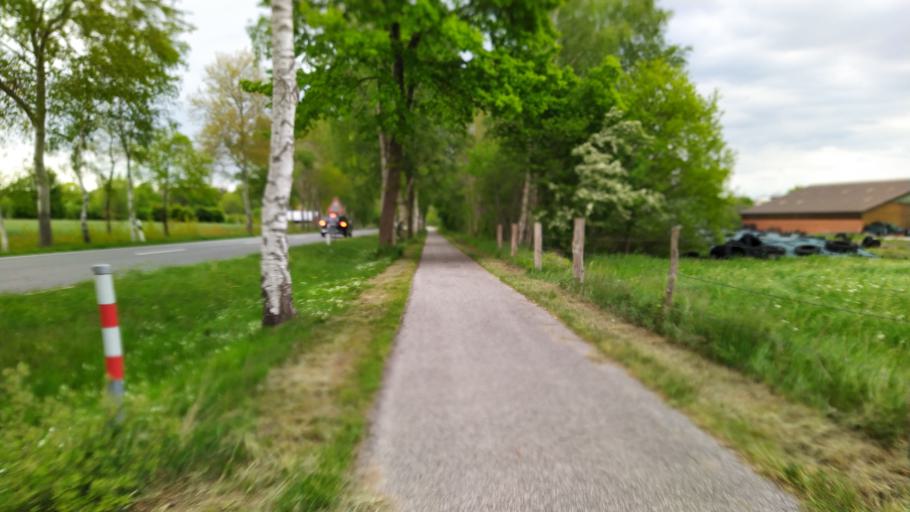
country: DE
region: Lower Saxony
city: Ostereistedt
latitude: 53.2684
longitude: 9.1970
